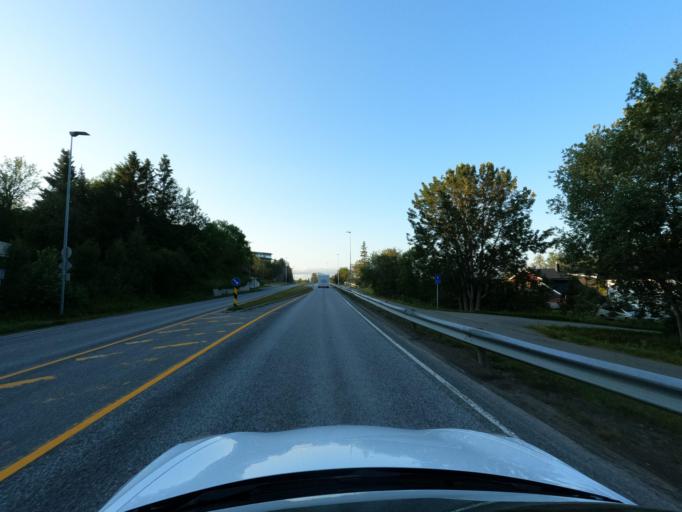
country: NO
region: Troms
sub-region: Harstad
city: Harstad
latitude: 68.7554
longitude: 16.5664
